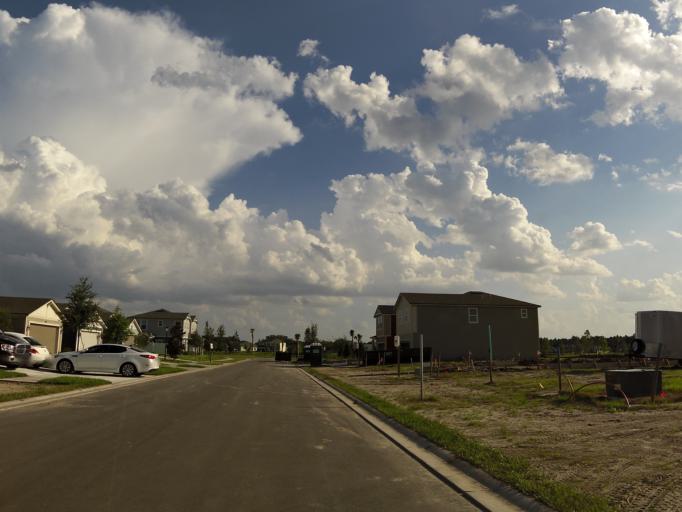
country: US
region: Florida
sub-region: Clay County
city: Green Cove Springs
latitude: 30.0311
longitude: -81.6308
